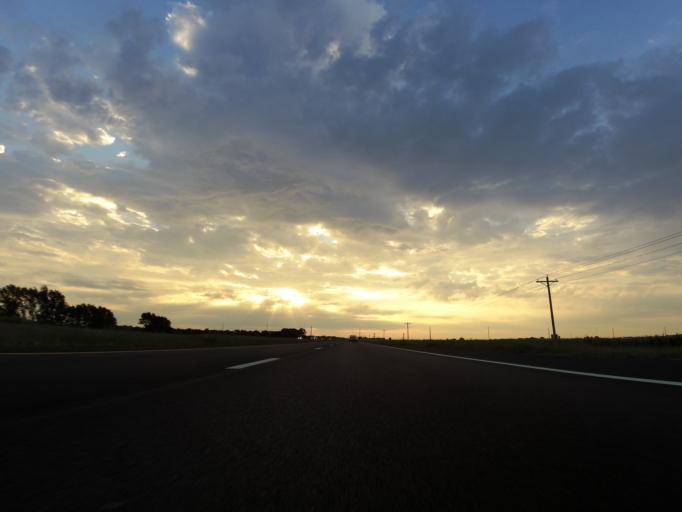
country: US
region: Kansas
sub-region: Sedgwick County
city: Colwich
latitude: 37.8248
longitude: -97.5353
